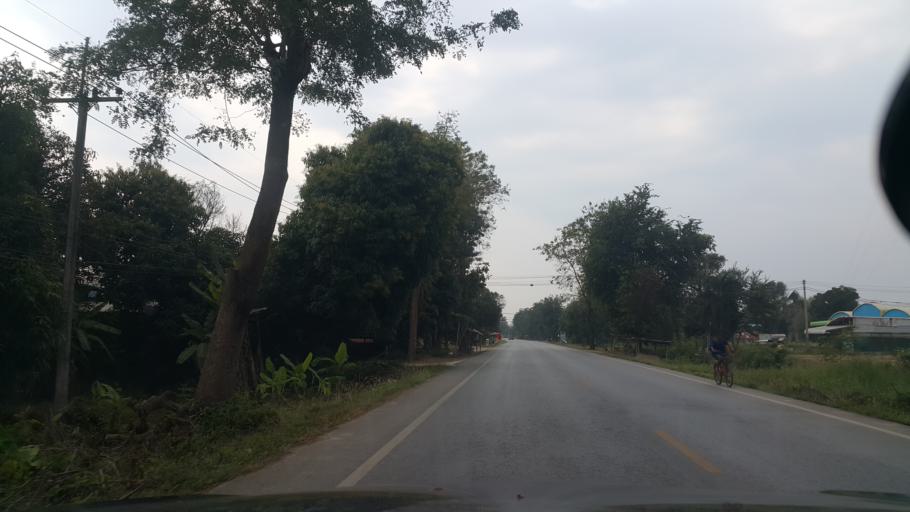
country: TH
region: Sukhothai
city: Si Samrong
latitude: 17.0999
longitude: 99.8859
